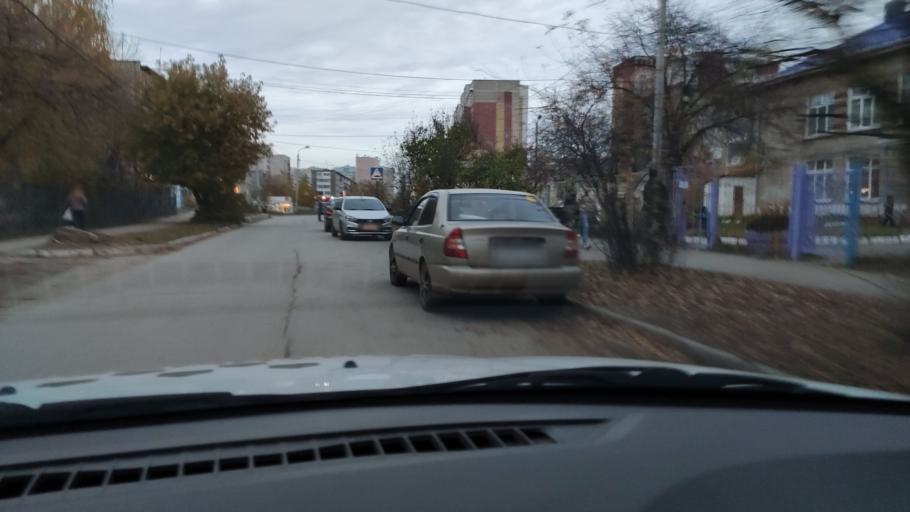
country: RU
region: Perm
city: Kondratovo
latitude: 58.0378
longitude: 56.1310
